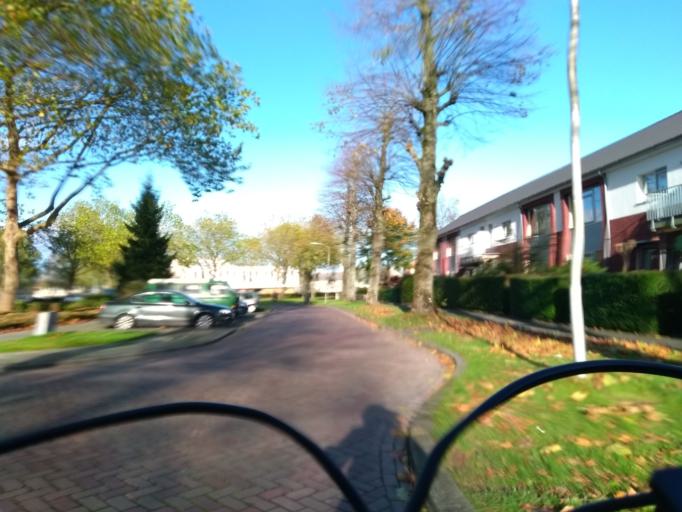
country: NL
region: Drenthe
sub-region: Gemeente Assen
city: Assen
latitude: 53.0016
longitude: 6.5631
